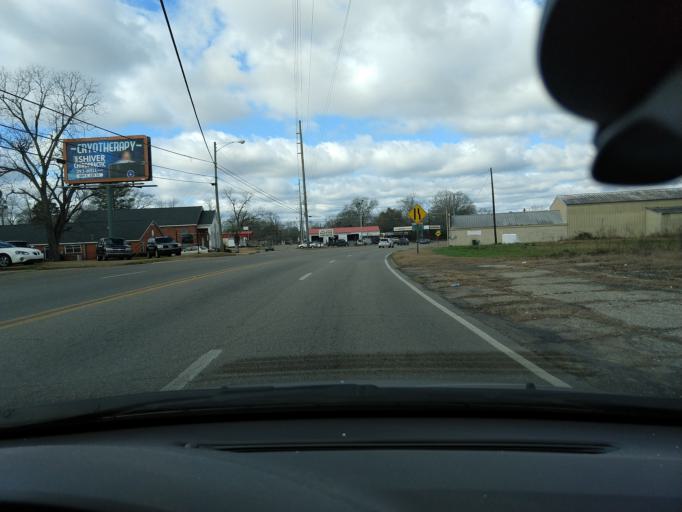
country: US
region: Alabama
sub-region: Coffee County
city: Enterprise
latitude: 31.3083
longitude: -85.8474
